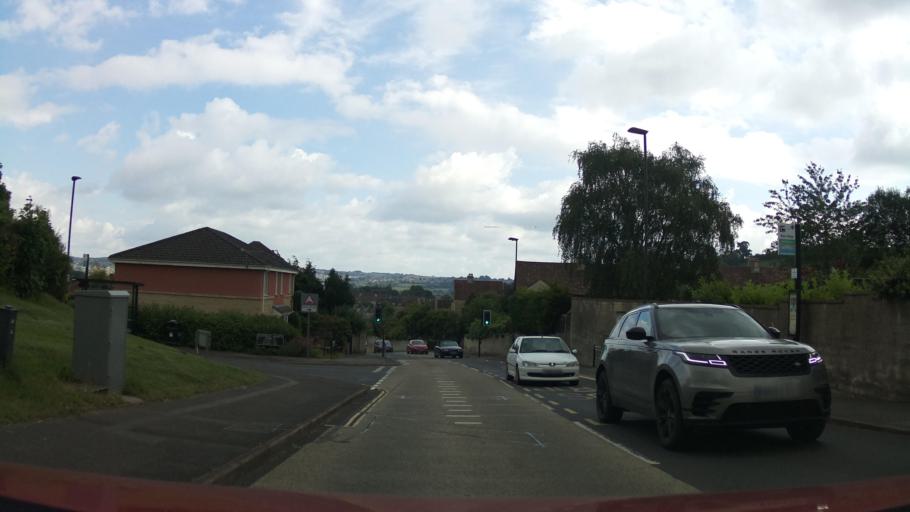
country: GB
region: England
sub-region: Bath and North East Somerset
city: Bath
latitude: 51.4016
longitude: -2.3958
